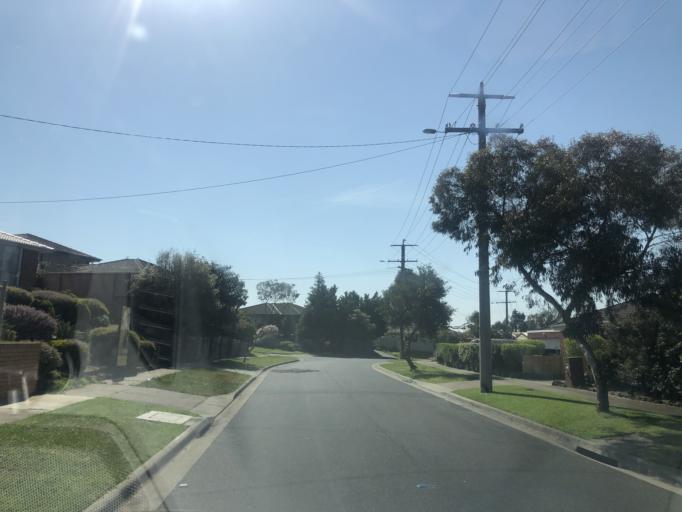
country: AU
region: Victoria
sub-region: Casey
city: Lynbrook
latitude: -38.0435
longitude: 145.2698
